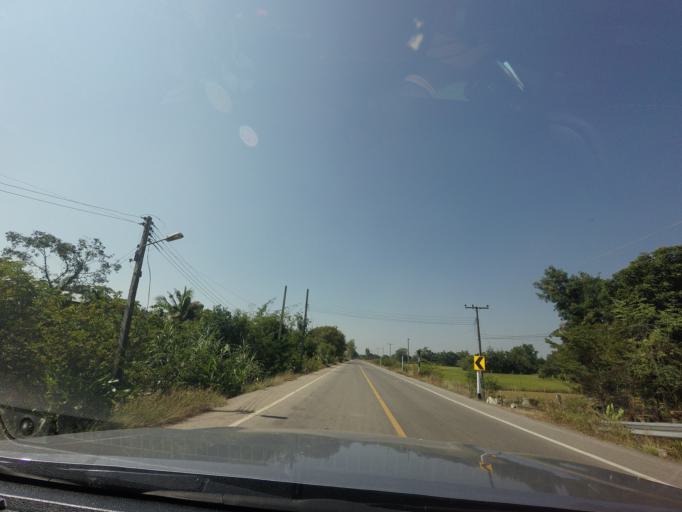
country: TH
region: Sukhothai
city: Si Samrong
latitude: 17.1351
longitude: 99.7748
